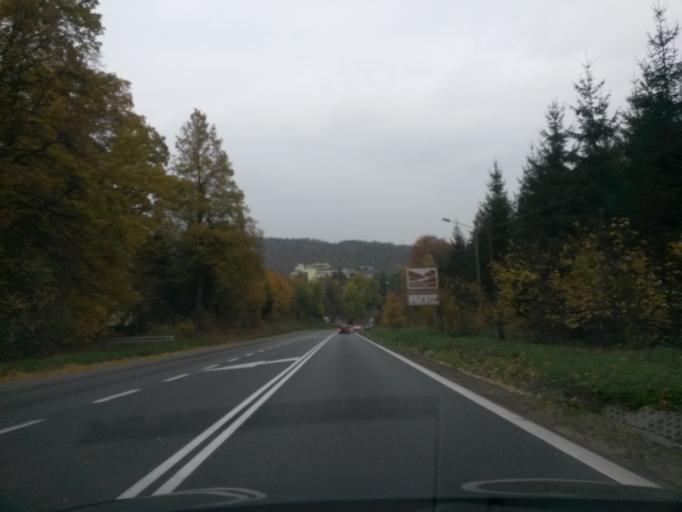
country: PL
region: Lower Silesian Voivodeship
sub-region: Powiat zabkowicki
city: Bardo
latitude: 50.5030
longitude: 16.7285
